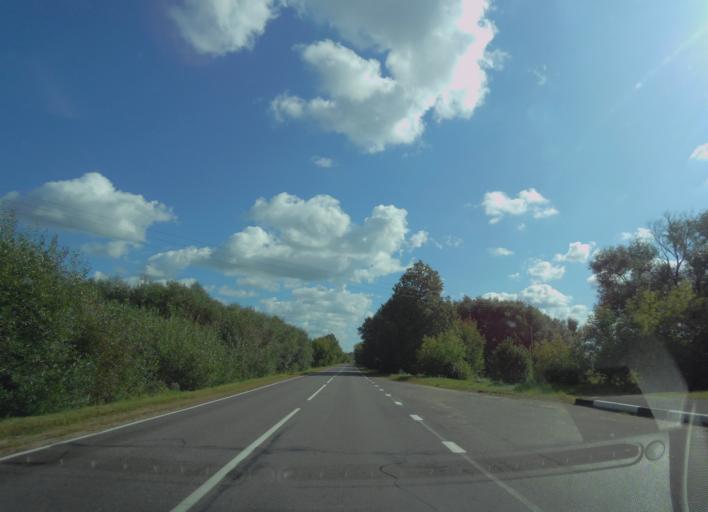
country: BY
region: Minsk
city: Zyembin
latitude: 54.3567
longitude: 28.3206
